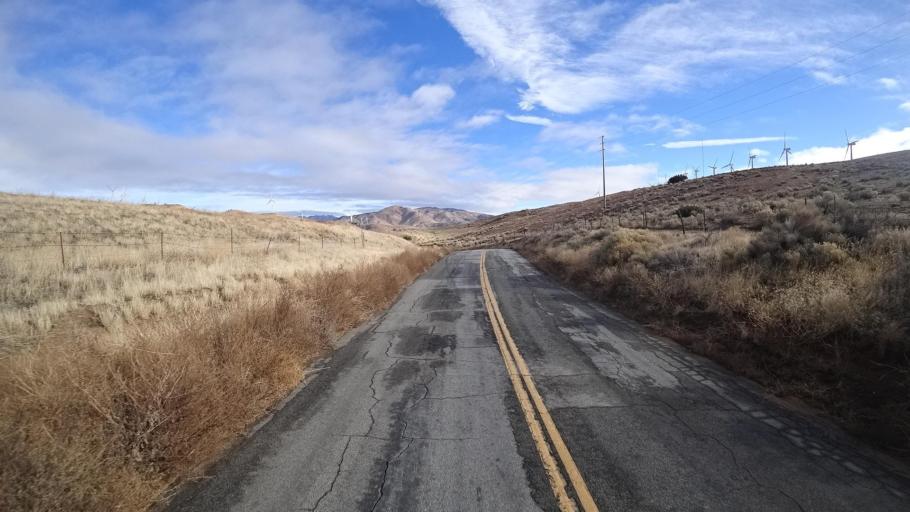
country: US
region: California
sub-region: Kern County
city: Tehachapi
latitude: 35.0714
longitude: -118.3433
